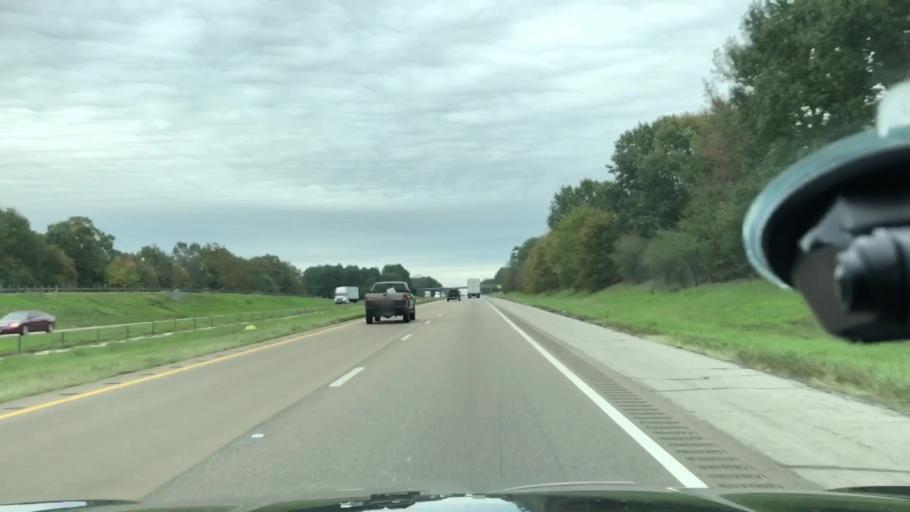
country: US
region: Texas
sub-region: Morris County
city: Omaha
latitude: 33.2605
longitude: -94.8322
